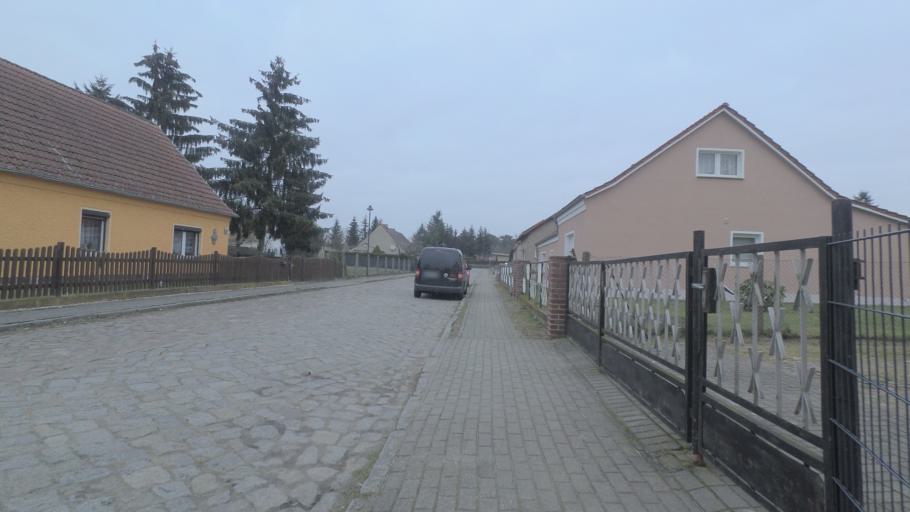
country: DE
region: Brandenburg
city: Ludwigsfelde
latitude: 52.3377
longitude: 13.2252
